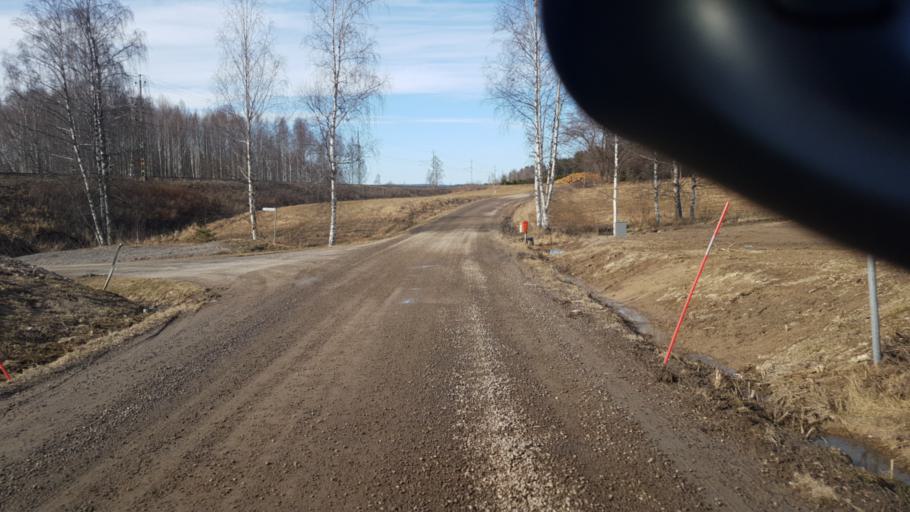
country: SE
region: Vaermland
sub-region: Eda Kommun
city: Amotfors
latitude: 59.7806
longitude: 12.3735
